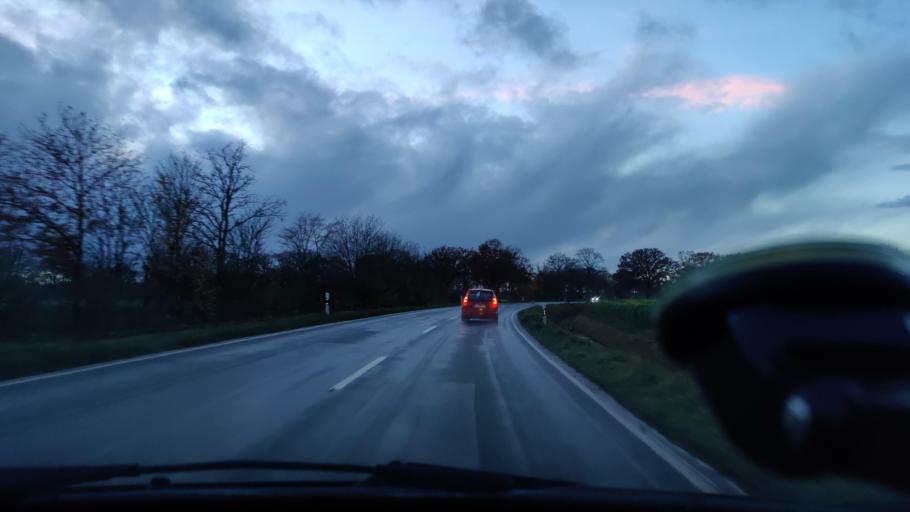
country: NL
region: Limburg
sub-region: Gemeente Bergen
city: Wellerlooi
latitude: 51.5682
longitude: 6.1596
